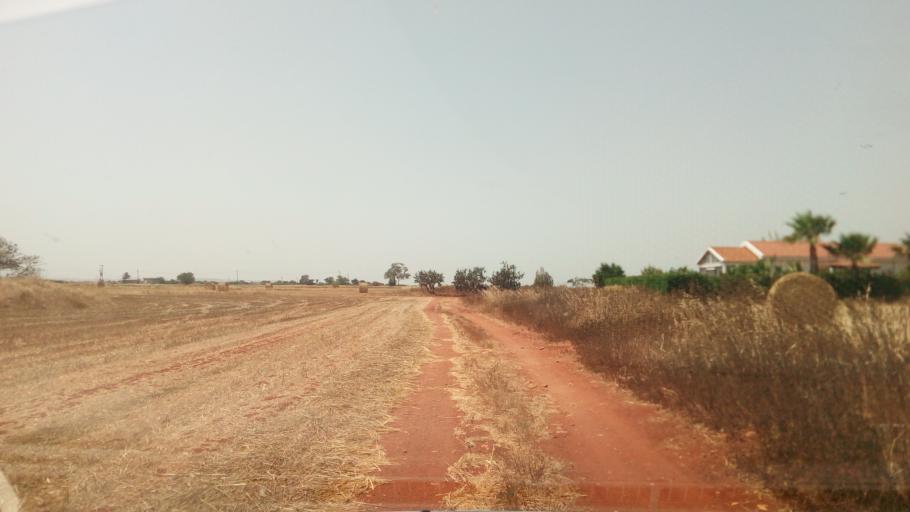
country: CY
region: Ammochostos
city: Avgorou
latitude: 35.0268
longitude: 33.8341
